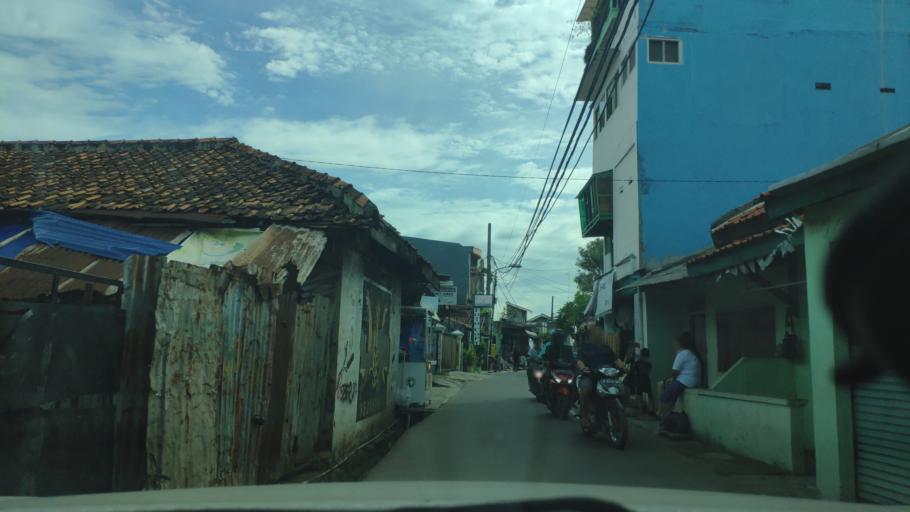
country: ID
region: West Java
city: Ciputat
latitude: -6.2222
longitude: 106.7133
